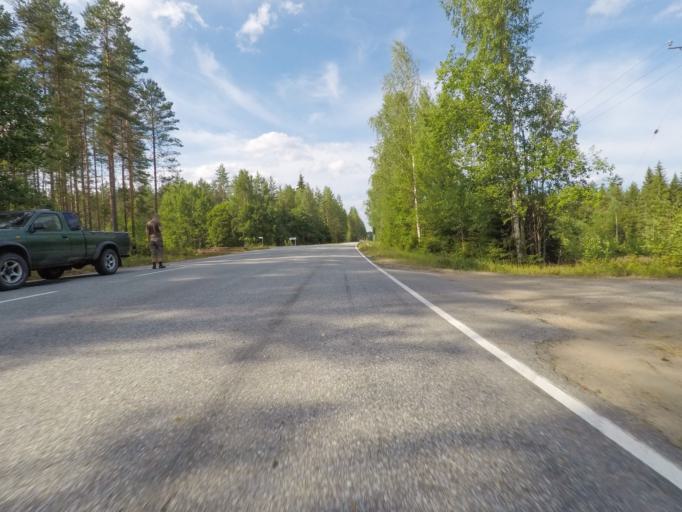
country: FI
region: Southern Savonia
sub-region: Savonlinna
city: Sulkava
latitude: 61.7216
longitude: 28.2058
